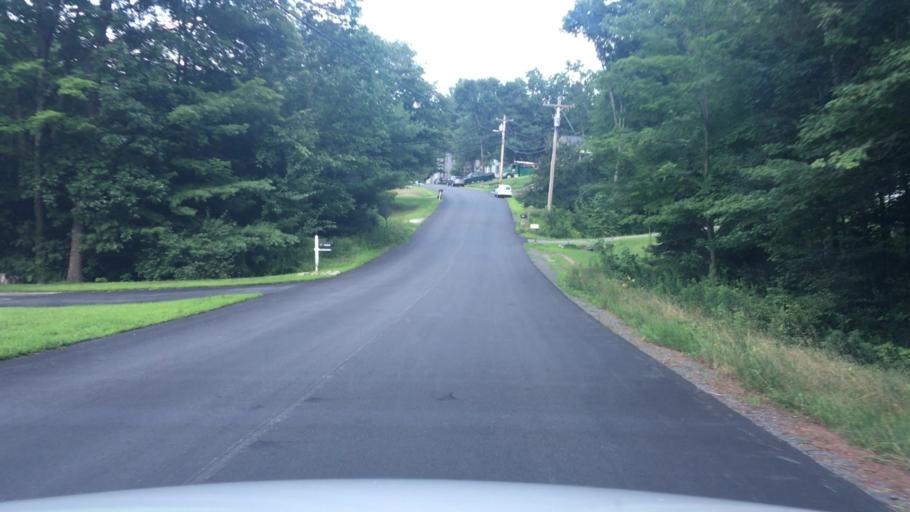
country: US
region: New Hampshire
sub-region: Rockingham County
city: Derry Village
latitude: 42.9373
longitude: -71.3392
